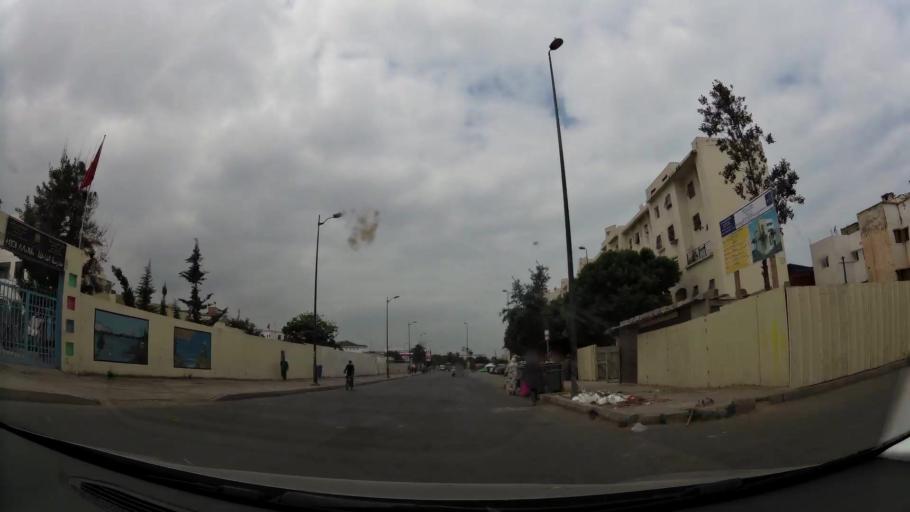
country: MA
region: Rabat-Sale-Zemmour-Zaer
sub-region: Rabat
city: Rabat
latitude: 33.9960
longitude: -6.8758
